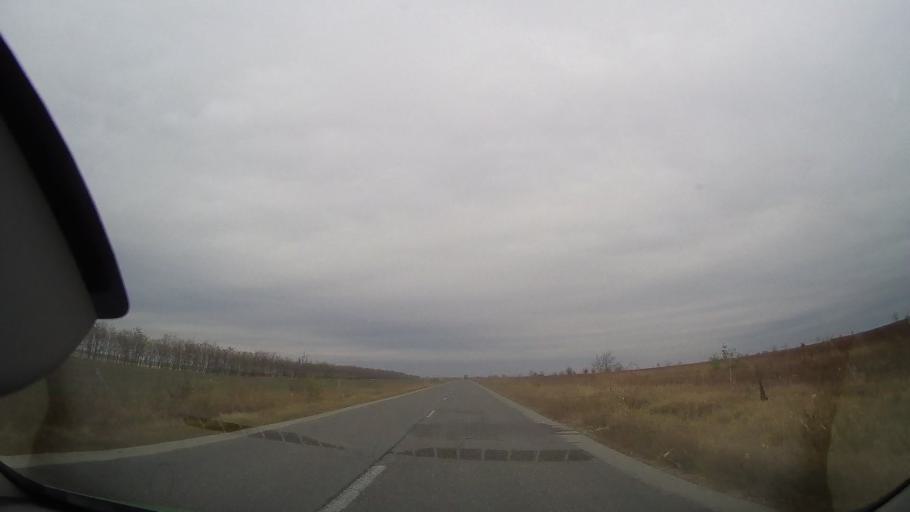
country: RO
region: Ialomita
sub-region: Comuna Milosesti
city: Milosesti
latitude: 44.7461
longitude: 27.2426
